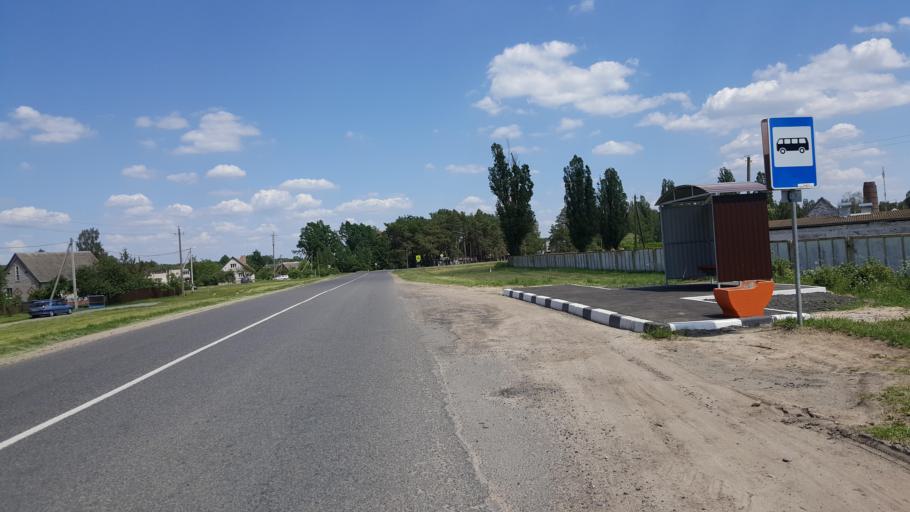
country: BY
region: Brest
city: Kobryn
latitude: 52.2298
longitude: 24.3045
